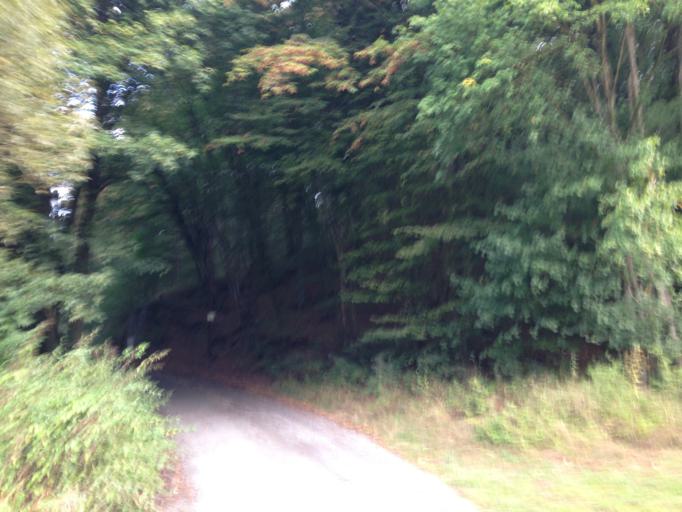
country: DE
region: Hesse
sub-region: Regierungsbezirk Giessen
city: Heuchelheim
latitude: 50.6386
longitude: 8.5655
